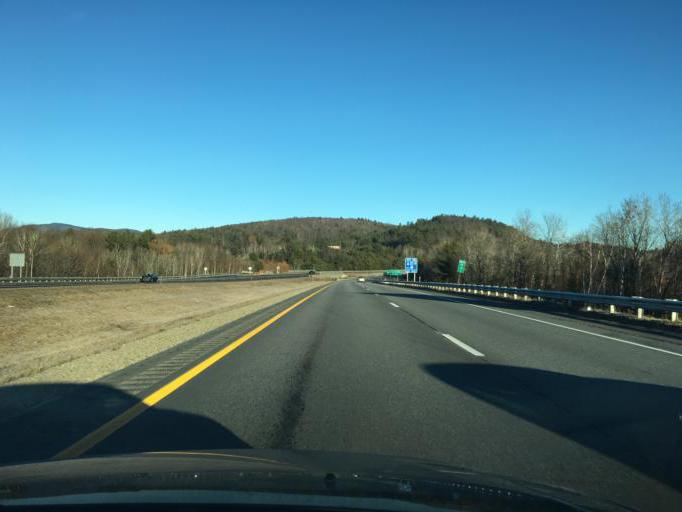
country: US
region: New Hampshire
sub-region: Grafton County
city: Plymouth
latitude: 43.7681
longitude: -71.6816
